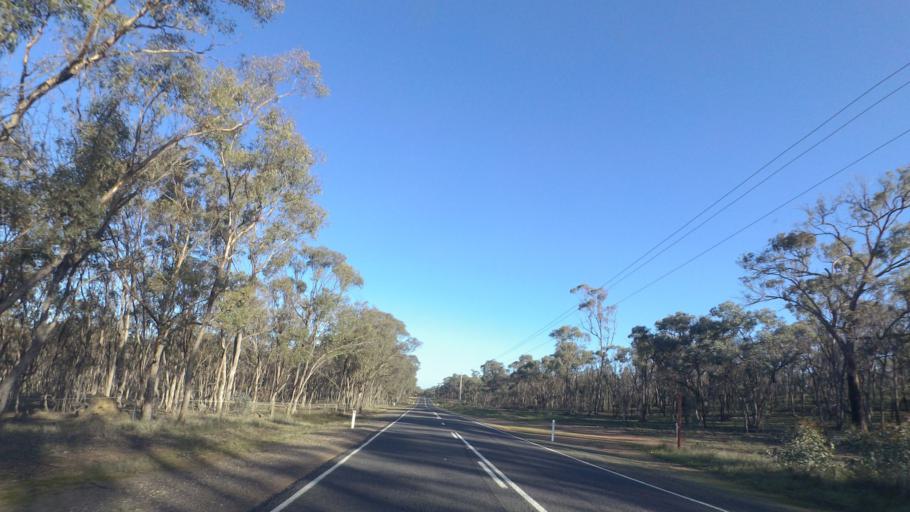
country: AU
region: Victoria
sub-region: Greater Bendigo
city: Kennington
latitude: -36.8807
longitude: 144.4929
